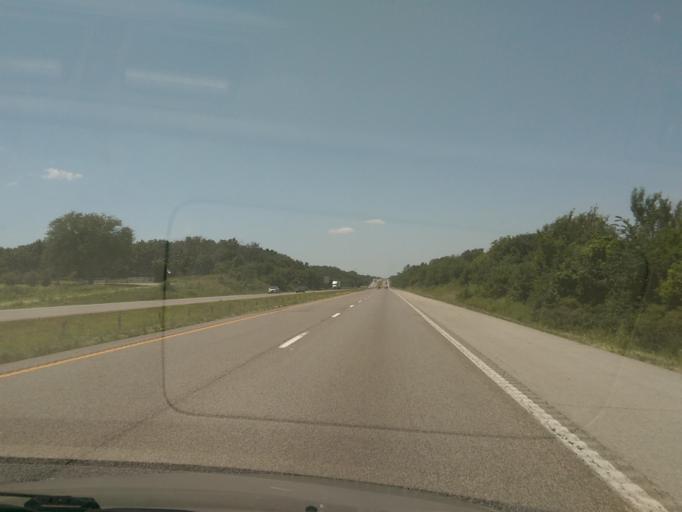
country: US
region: Missouri
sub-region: Saline County
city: Marshall
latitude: 38.9546
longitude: -93.1092
